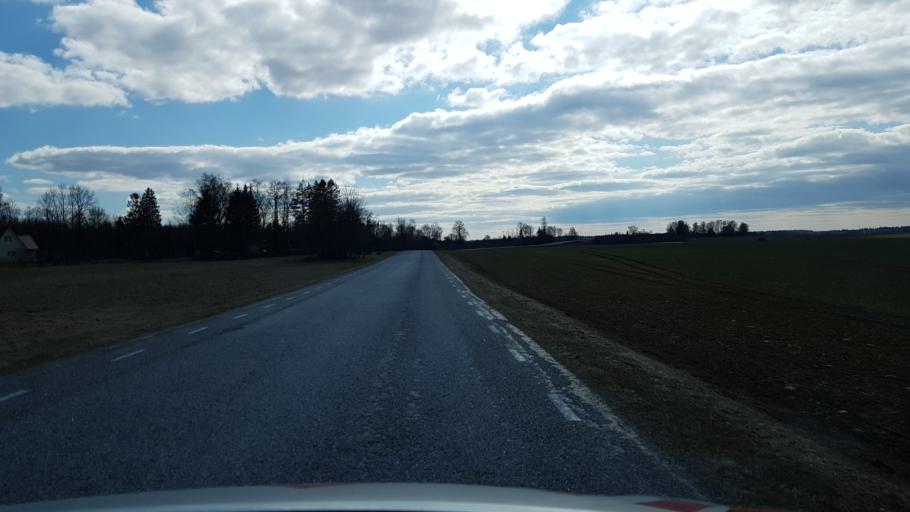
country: EE
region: Laeaene-Virumaa
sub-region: Kadrina vald
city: Kadrina
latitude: 59.2985
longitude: 26.2157
